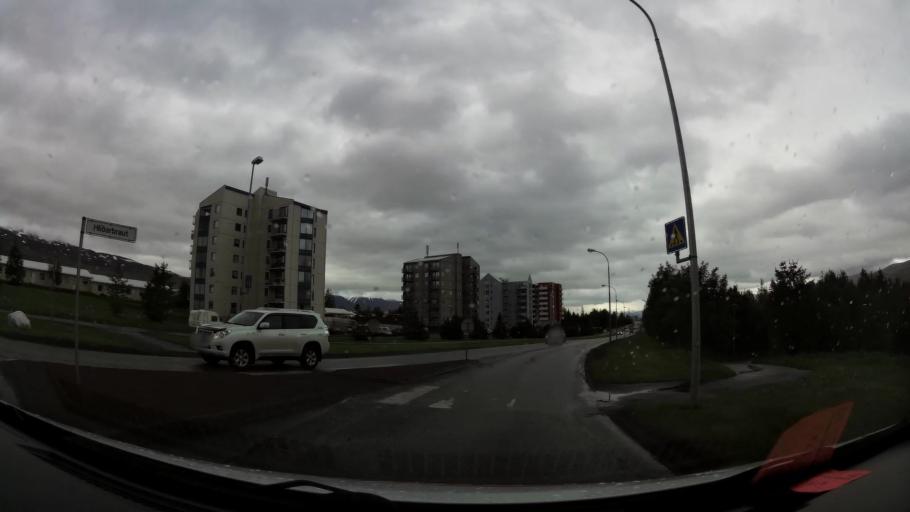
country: IS
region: Northeast
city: Akureyri
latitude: 65.6845
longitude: -18.1294
